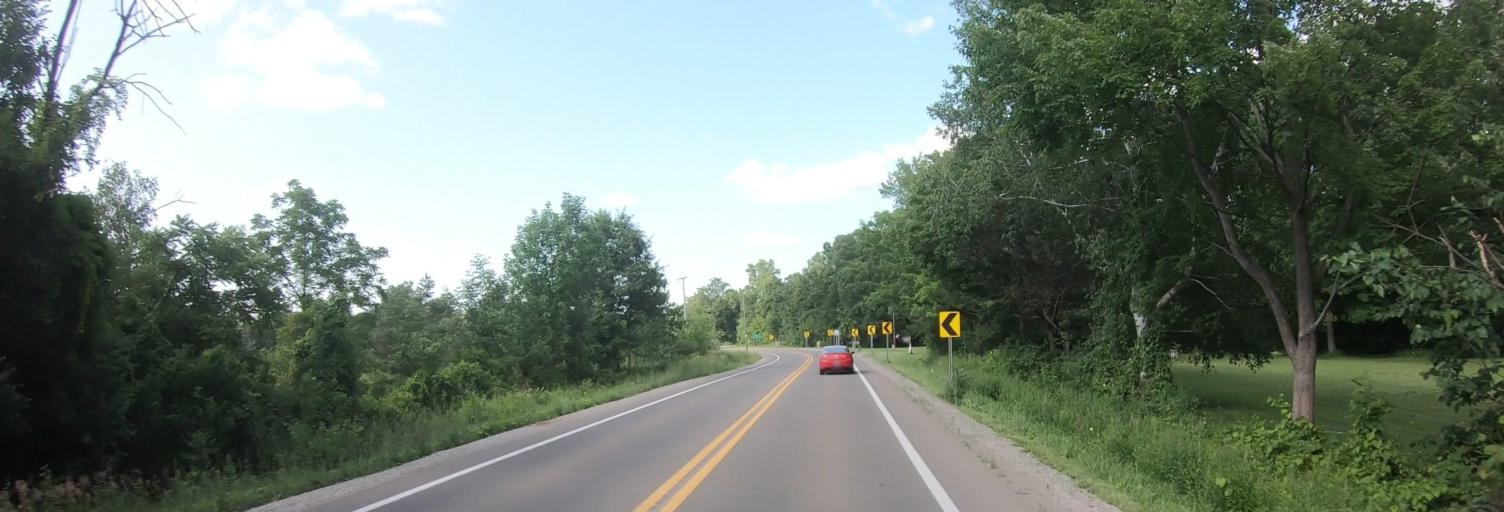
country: US
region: Michigan
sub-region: Oakland County
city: Holly
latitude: 42.8352
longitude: -83.6298
